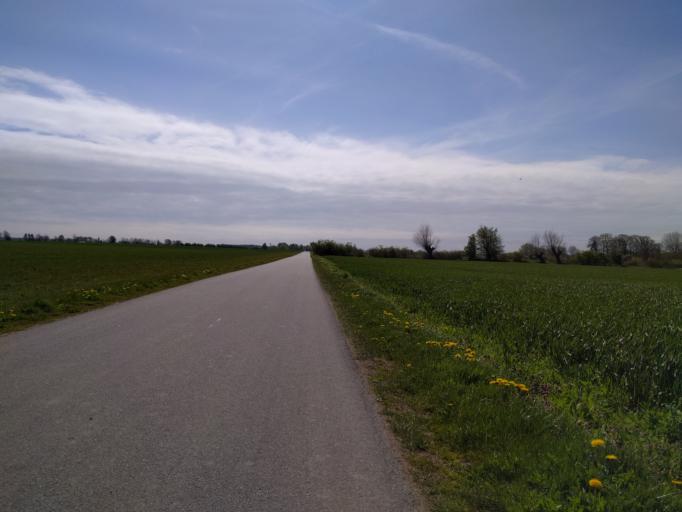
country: DK
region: South Denmark
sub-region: Kerteminde Kommune
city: Munkebo
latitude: 55.4452
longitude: 10.5895
